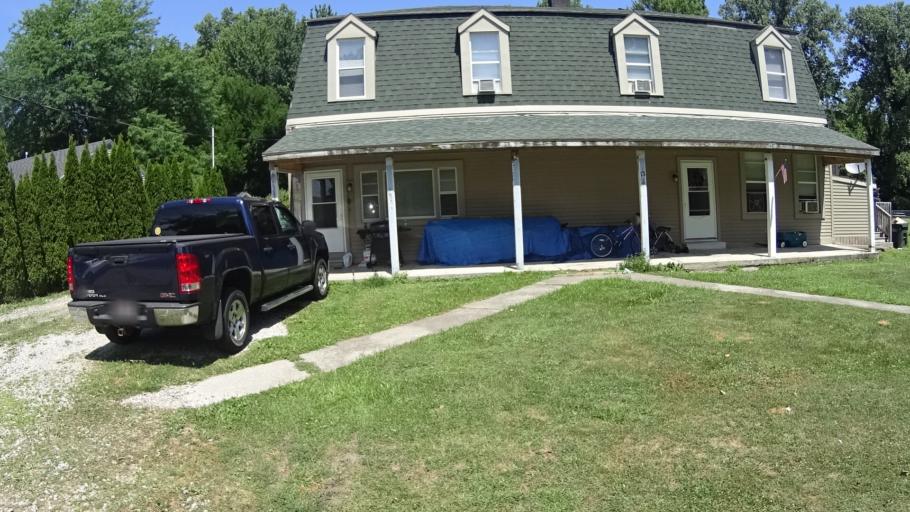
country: US
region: Ohio
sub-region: Erie County
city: Sandusky
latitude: 41.4040
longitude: -82.8156
